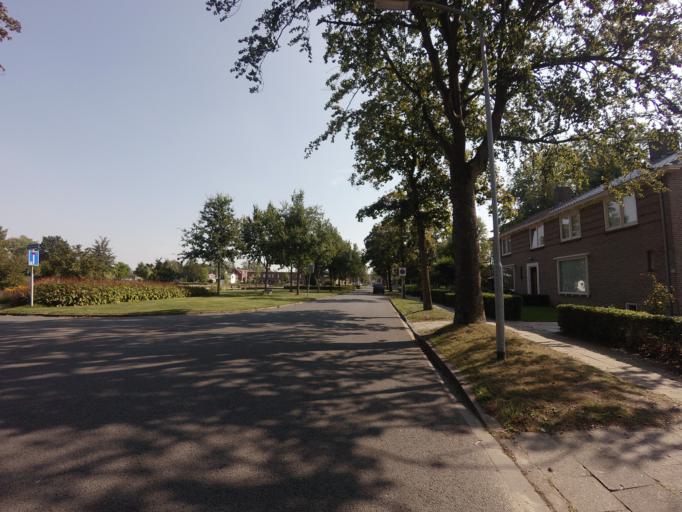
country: NL
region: Groningen
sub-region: Gemeente Zuidhorn
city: Zuidhorn
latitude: 53.2460
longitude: 6.4096
